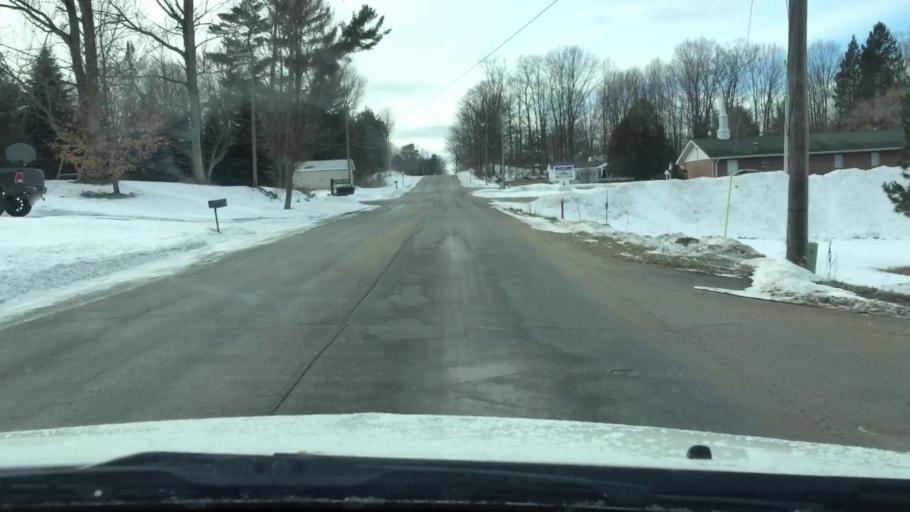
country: US
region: Michigan
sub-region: Wexford County
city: Manton
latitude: 44.4037
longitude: -85.4019
